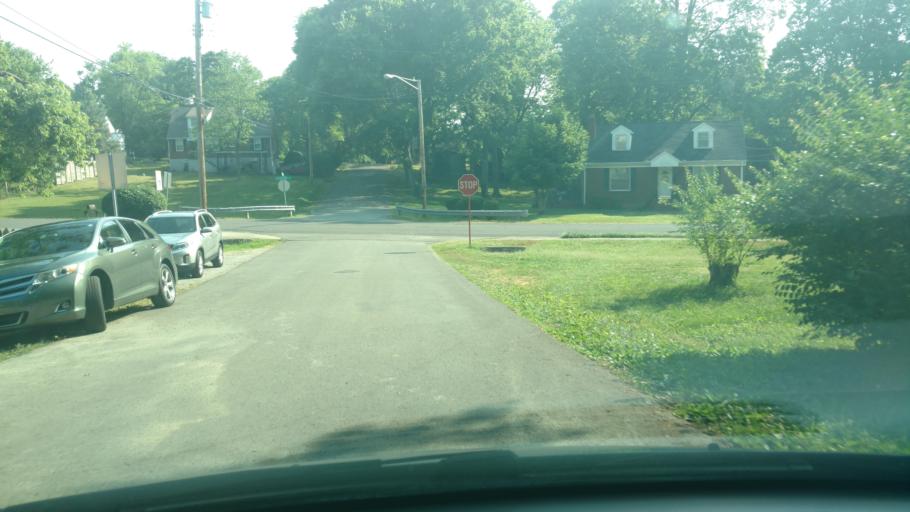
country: US
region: Tennessee
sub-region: Davidson County
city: Lakewood
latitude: 36.2179
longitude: -86.7152
